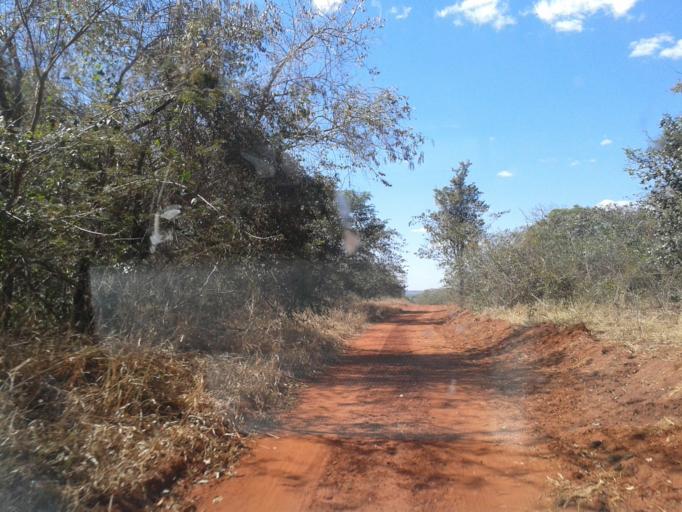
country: BR
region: Minas Gerais
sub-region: Santa Vitoria
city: Santa Vitoria
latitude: -19.0182
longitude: -50.4493
